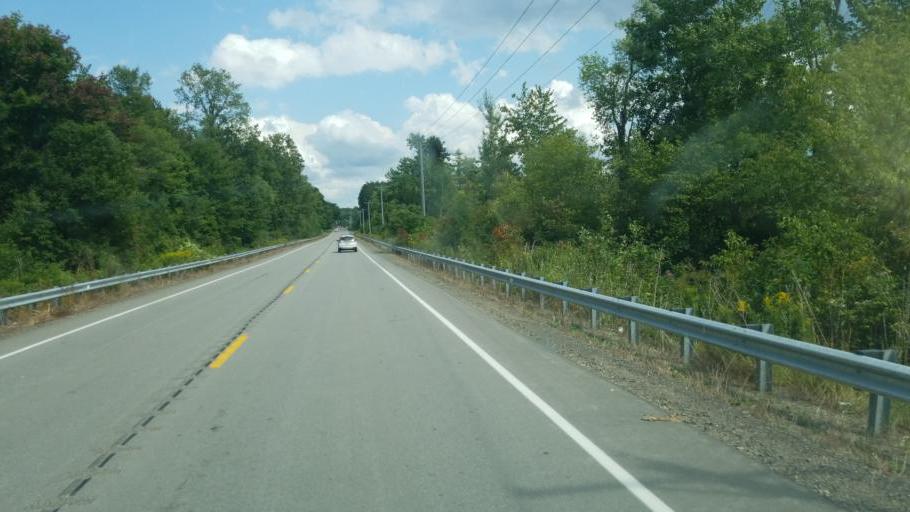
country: US
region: Pennsylvania
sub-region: Crawford County
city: Linesville
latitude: 41.6055
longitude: -80.3892
